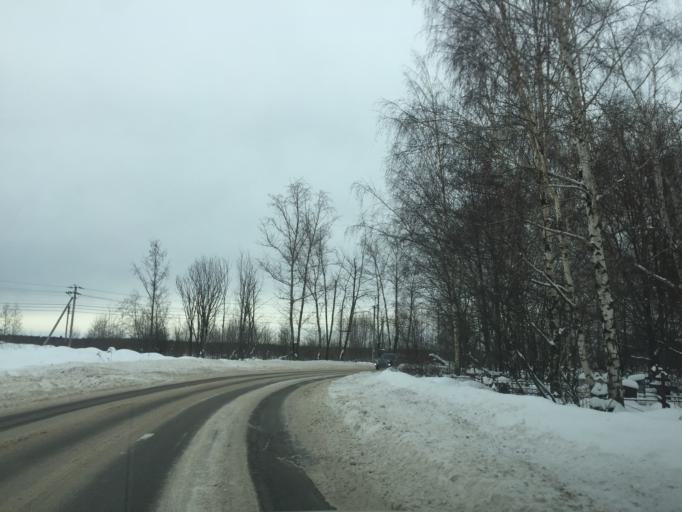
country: RU
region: Leningrad
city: Imeni Sverdlova
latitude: 59.7913
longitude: 30.6873
